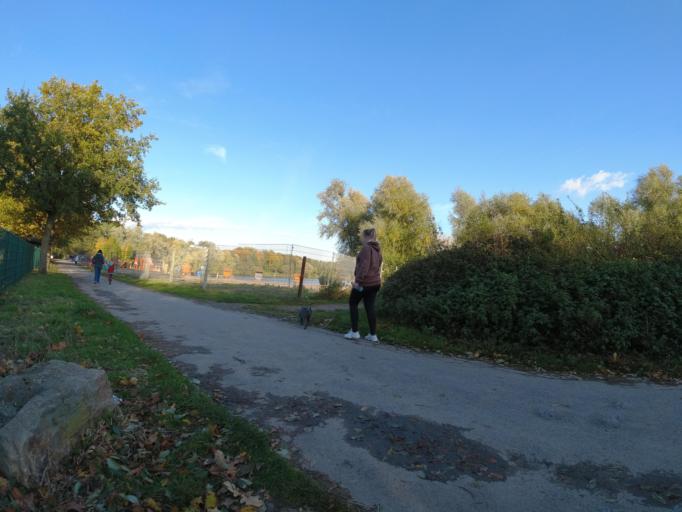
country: DE
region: North Rhine-Westphalia
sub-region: Regierungsbezirk Dusseldorf
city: Moers
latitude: 51.4064
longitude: 6.6701
